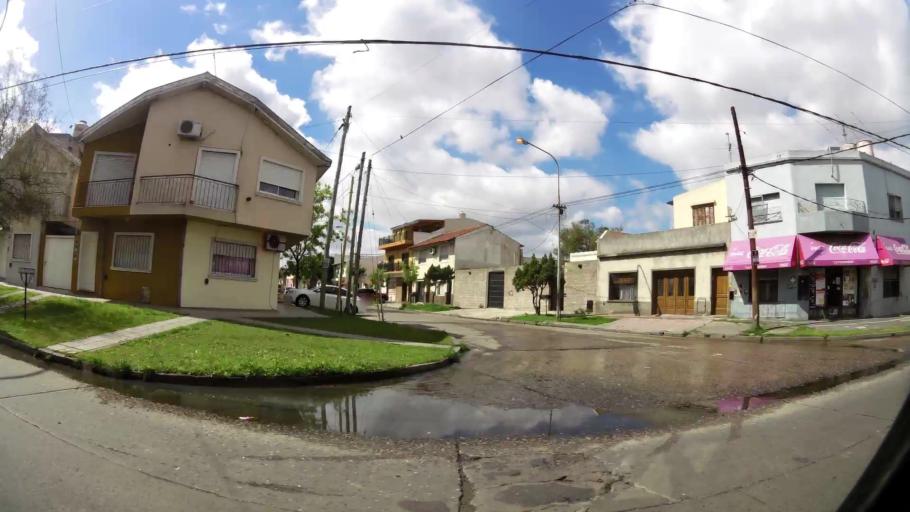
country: AR
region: Buenos Aires
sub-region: Partido de Lanus
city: Lanus
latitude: -34.6866
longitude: -58.4128
